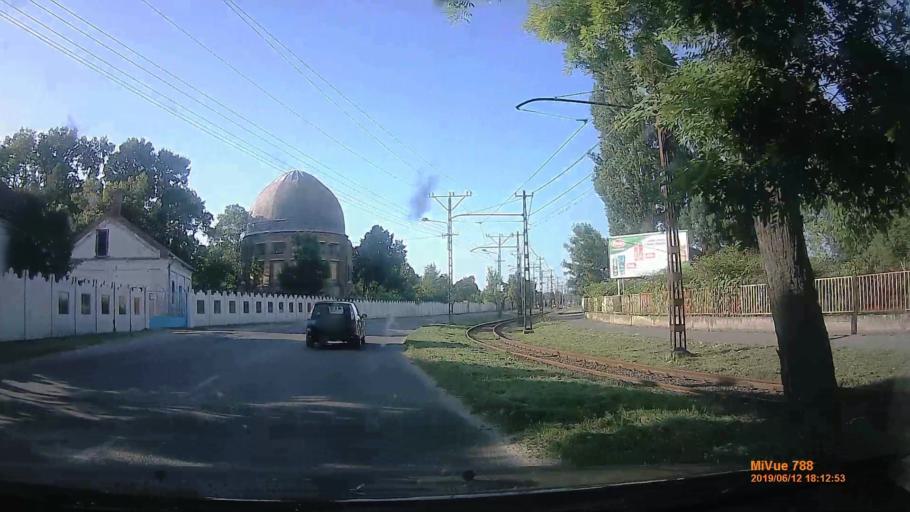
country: HU
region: Csongrad
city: Szeged
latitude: 46.2571
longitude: 20.1059
